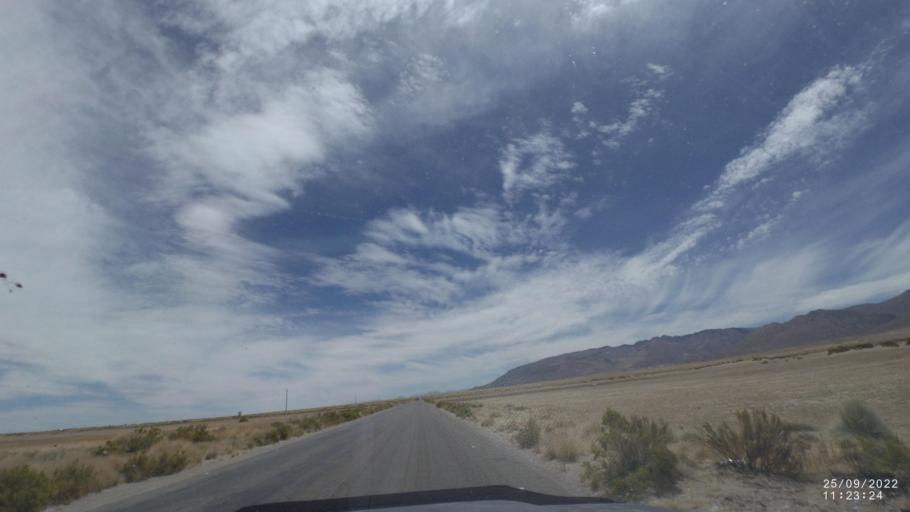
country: BO
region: Oruro
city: Challapata
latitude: -19.1101
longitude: -66.7708
